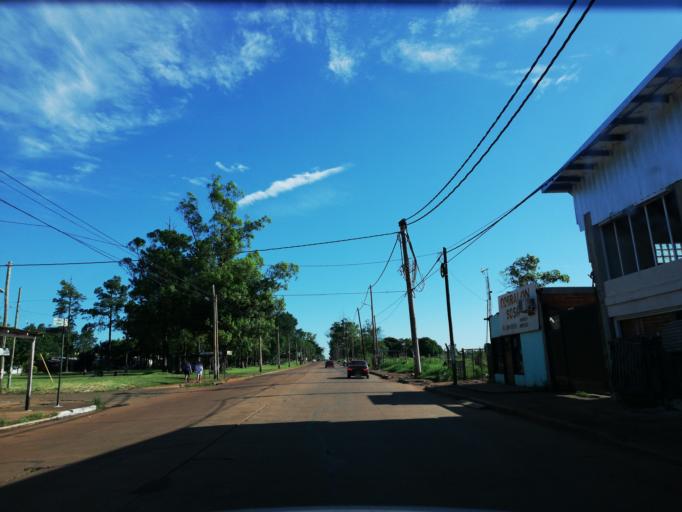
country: AR
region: Misiones
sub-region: Departamento de Capital
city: Posadas
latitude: -27.4014
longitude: -55.9522
